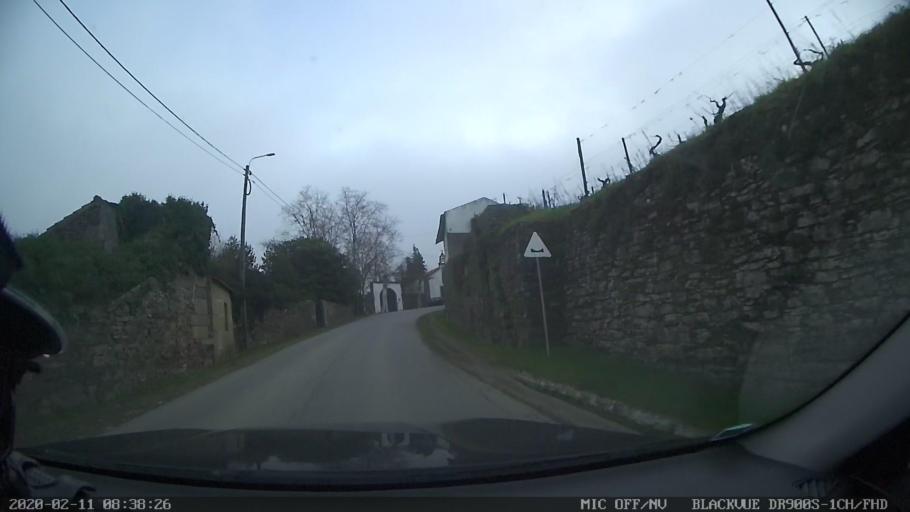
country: PT
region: Vila Real
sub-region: Sabrosa
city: Sabrosa
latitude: 41.2497
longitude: -7.5841
